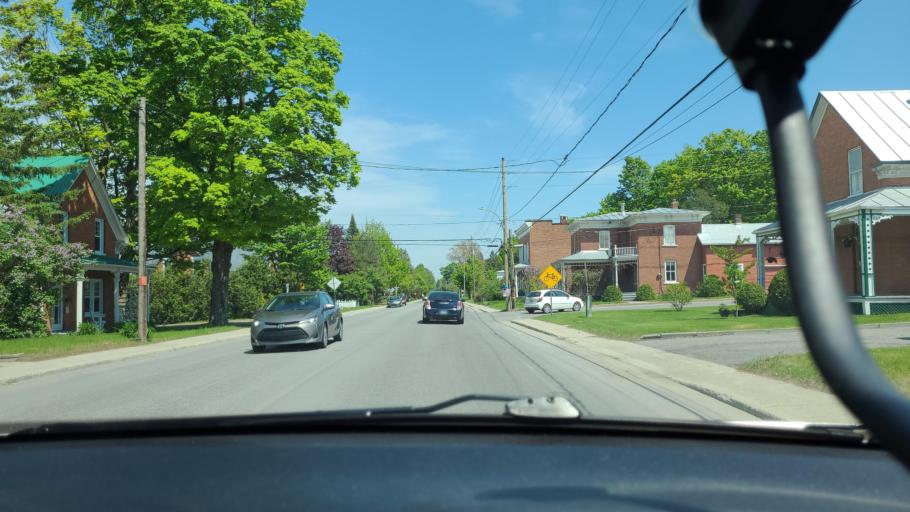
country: CA
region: Quebec
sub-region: Laurentides
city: Lachute
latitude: 45.6582
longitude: -74.3276
